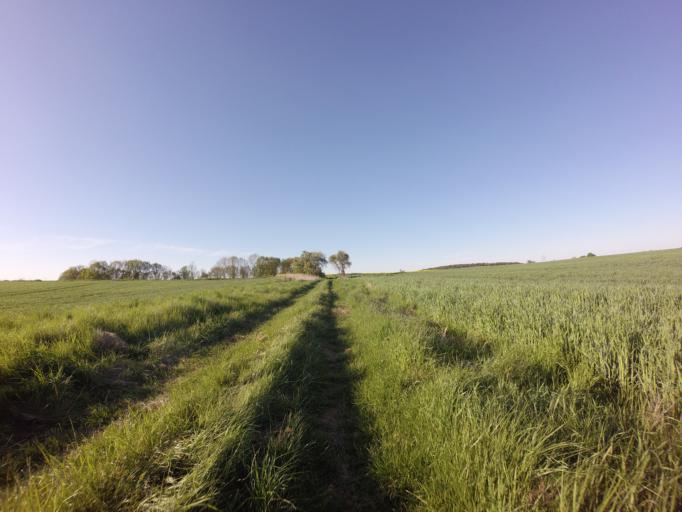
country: PL
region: West Pomeranian Voivodeship
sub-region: Powiat choszczenski
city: Choszczno
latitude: 53.1516
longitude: 15.3688
